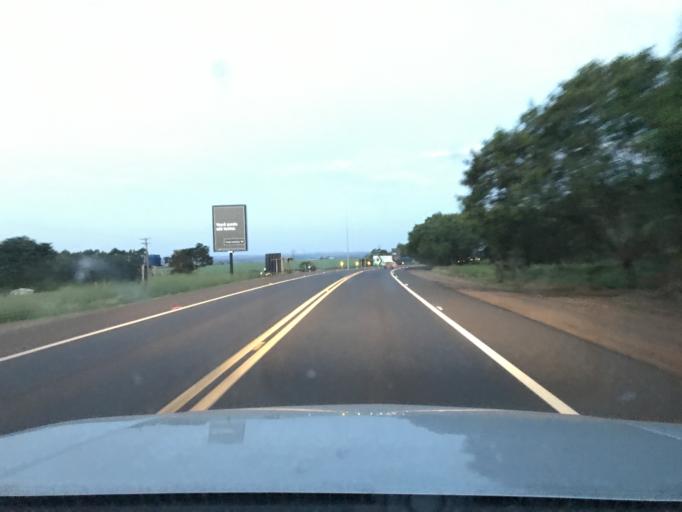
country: PY
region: Canindeyu
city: Salto del Guaira
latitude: -24.0121
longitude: -54.3027
